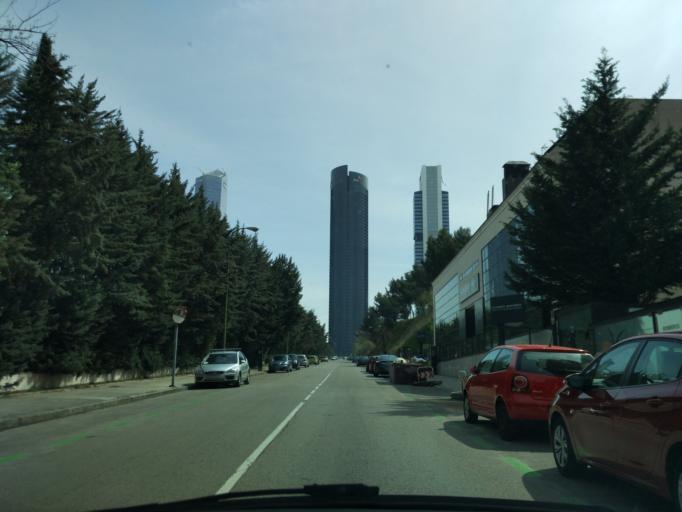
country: ES
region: Madrid
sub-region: Provincia de Madrid
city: Tetuan de las Victorias
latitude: 40.4777
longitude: -3.6966
